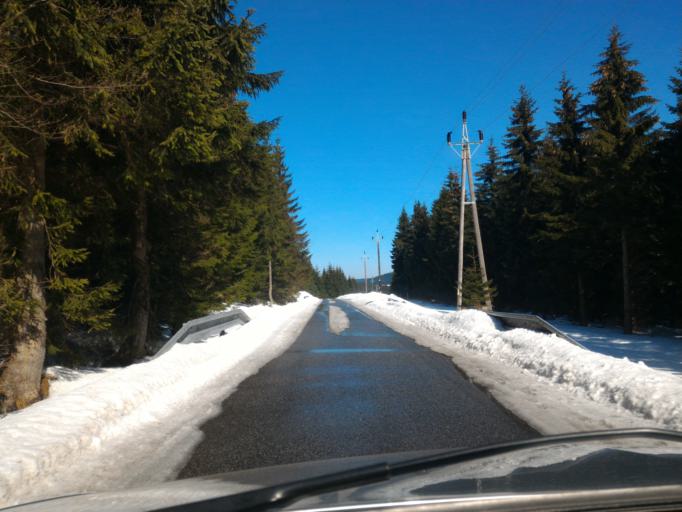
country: CZ
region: Liberecky
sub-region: Okres Jablonec nad Nisou
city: Korenov
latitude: 50.7950
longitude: 15.3528
